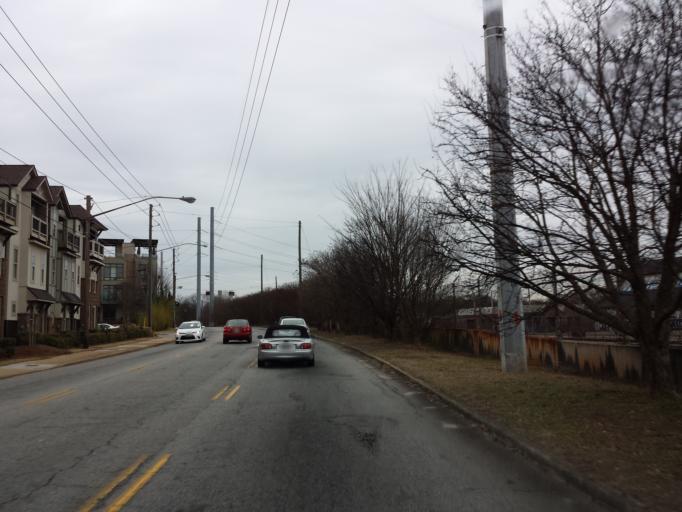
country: US
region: Georgia
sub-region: DeKalb County
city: Druid Hills
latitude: 33.7606
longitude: -84.3291
